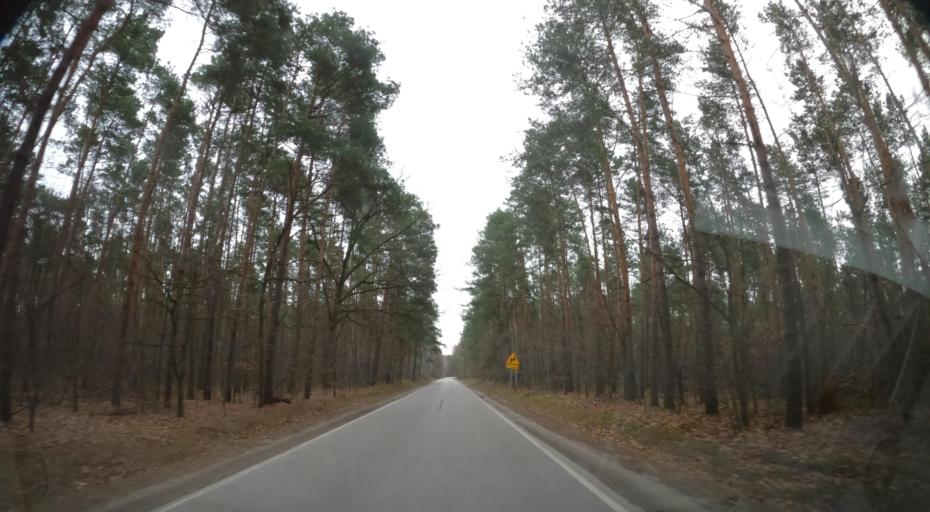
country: PL
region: Masovian Voivodeship
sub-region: Powiat radomski
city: Jedlinsk
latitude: 51.4920
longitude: 21.1574
